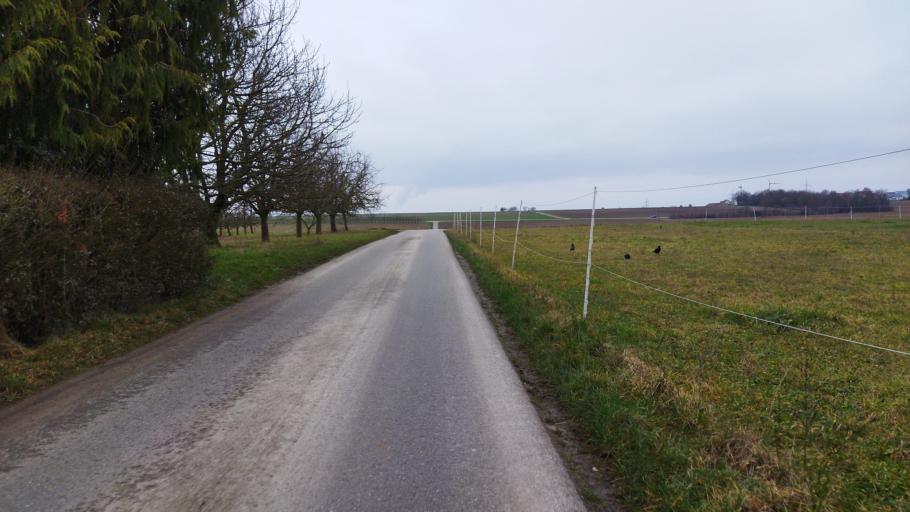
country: DE
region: Baden-Wuerttemberg
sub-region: Regierungsbezirk Stuttgart
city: Nordheim
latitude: 49.1310
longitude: 9.1579
